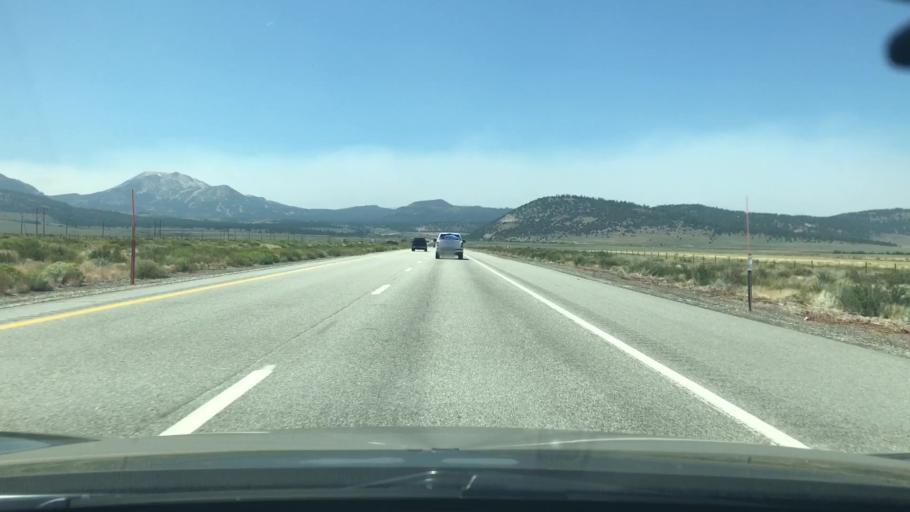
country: US
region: California
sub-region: Mono County
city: Mammoth Lakes
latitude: 37.6264
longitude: -118.8523
